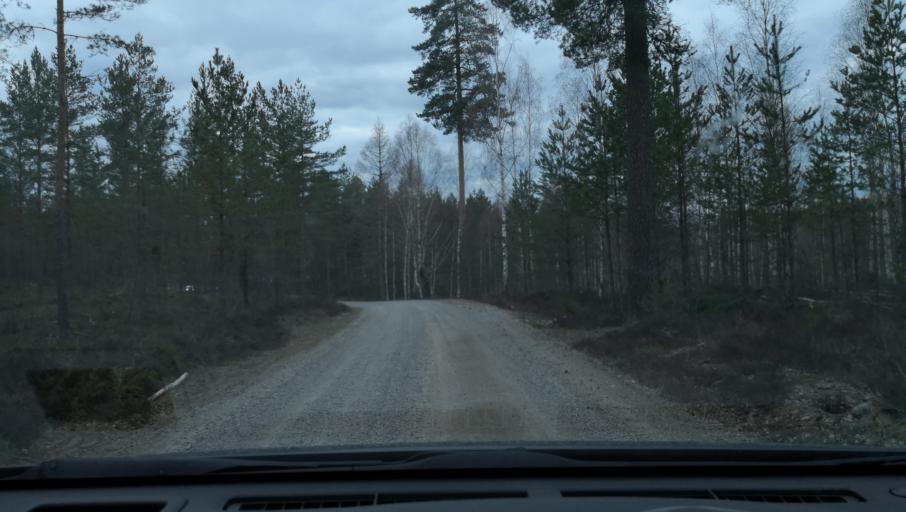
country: SE
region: Soedermanland
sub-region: Katrineholms Kommun
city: Katrineholm
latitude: 59.1337
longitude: 16.1470
